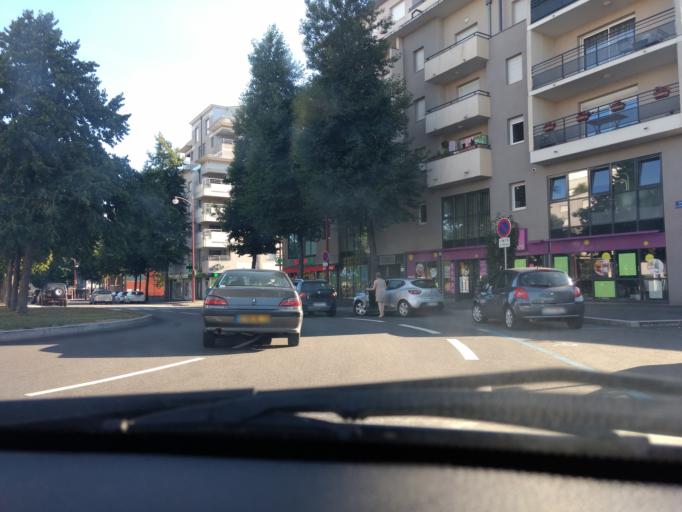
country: FR
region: Midi-Pyrenees
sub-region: Departement de l'Aveyron
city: Olemps
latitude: 44.3611
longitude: 2.5562
